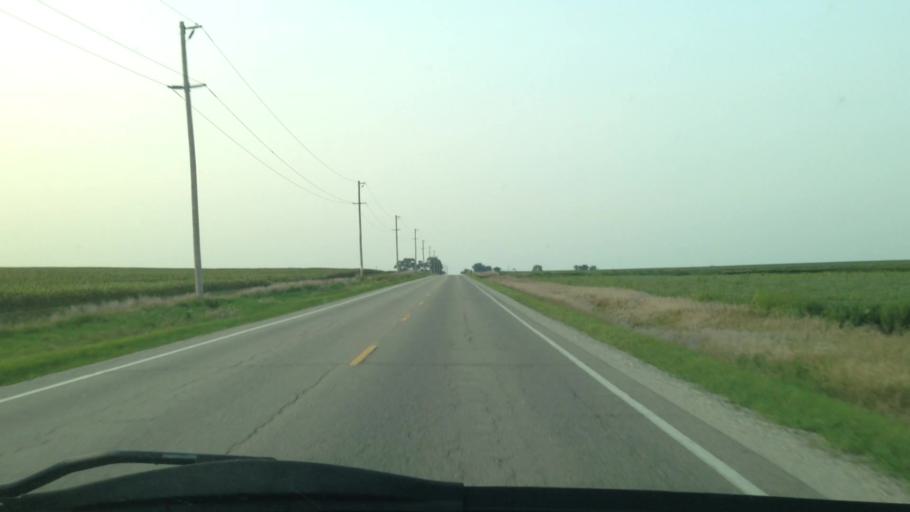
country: US
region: Iowa
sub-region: Iowa County
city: Marengo
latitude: 41.9548
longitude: -92.0852
